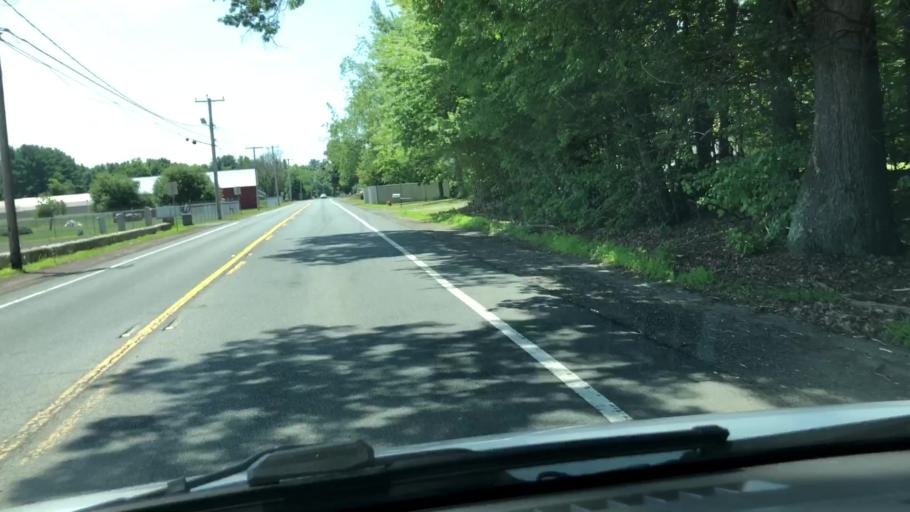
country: US
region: Massachusetts
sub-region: Franklin County
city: Whately
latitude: 42.4187
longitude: -72.6213
